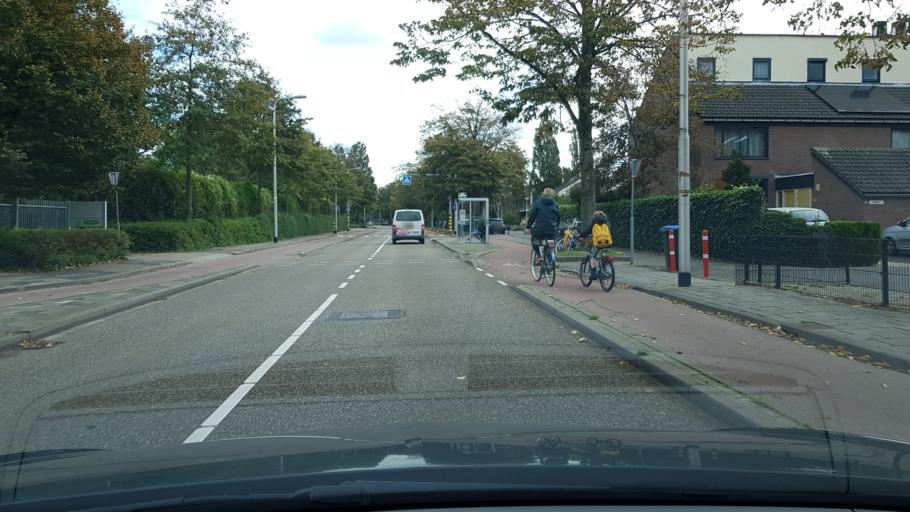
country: NL
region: South Holland
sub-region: Gemeente Hillegom
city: Hillegom
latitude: 52.2867
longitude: 4.5807
